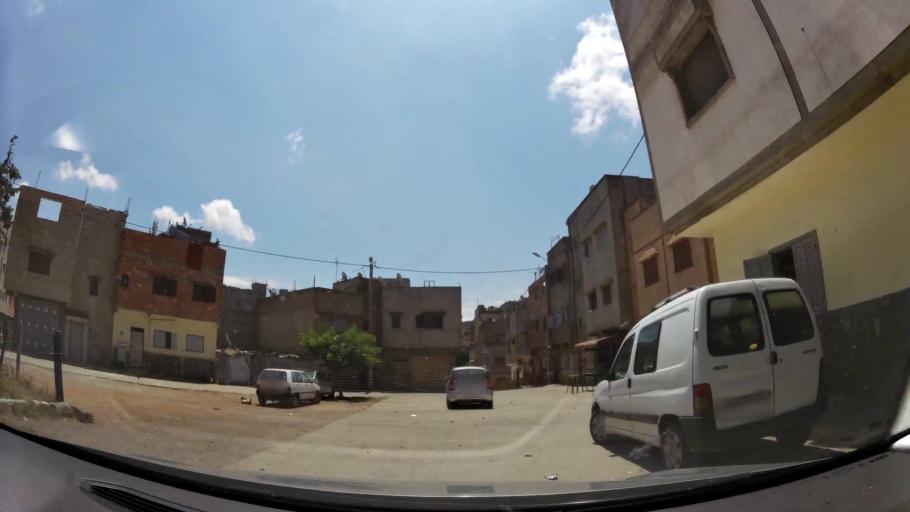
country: MA
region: Rabat-Sale-Zemmour-Zaer
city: Sale
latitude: 34.0694
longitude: -6.7831
